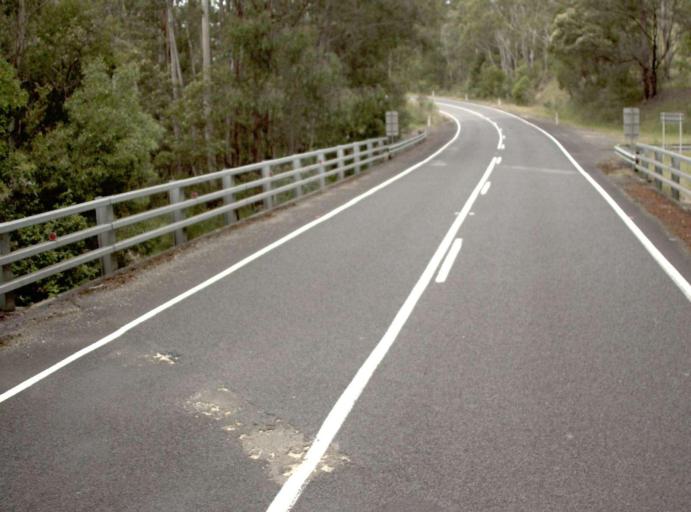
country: AU
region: New South Wales
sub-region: Bombala
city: Bombala
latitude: -37.2831
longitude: 149.2223
